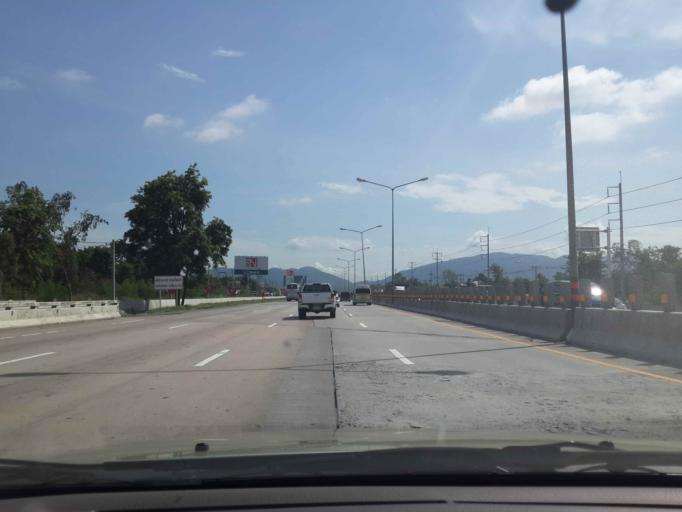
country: TH
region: Chon Buri
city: Si Racha
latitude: 13.1863
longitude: 100.9972
